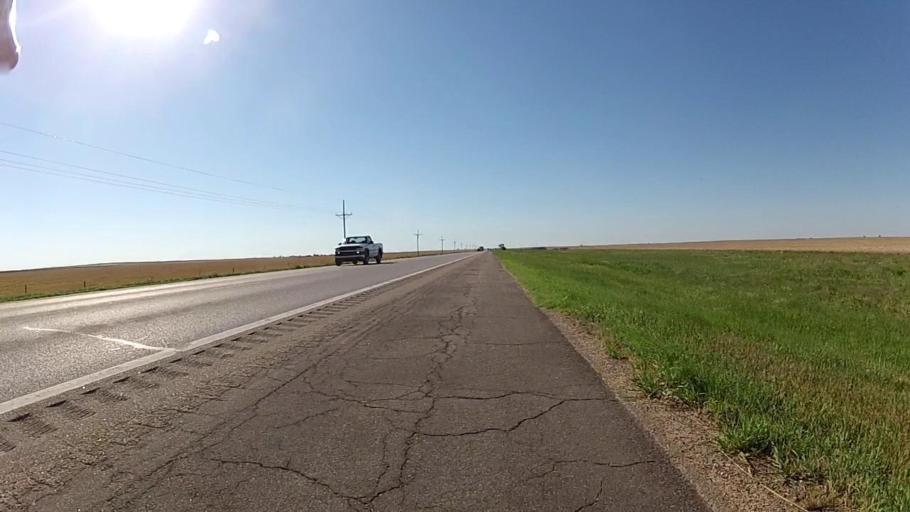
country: US
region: Kansas
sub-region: Ford County
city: Dodge City
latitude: 37.6008
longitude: -99.7015
